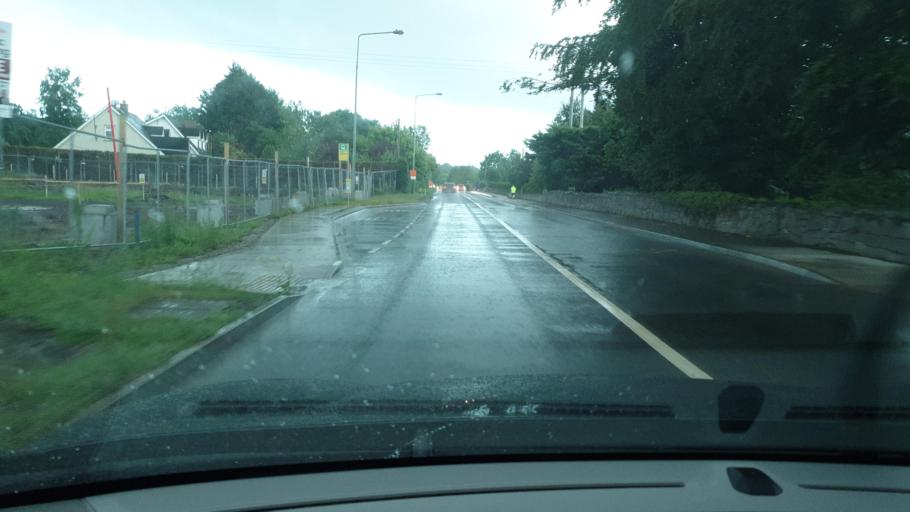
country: IE
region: Leinster
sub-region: An Mhi
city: Navan
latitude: 53.6411
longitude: -6.6886
